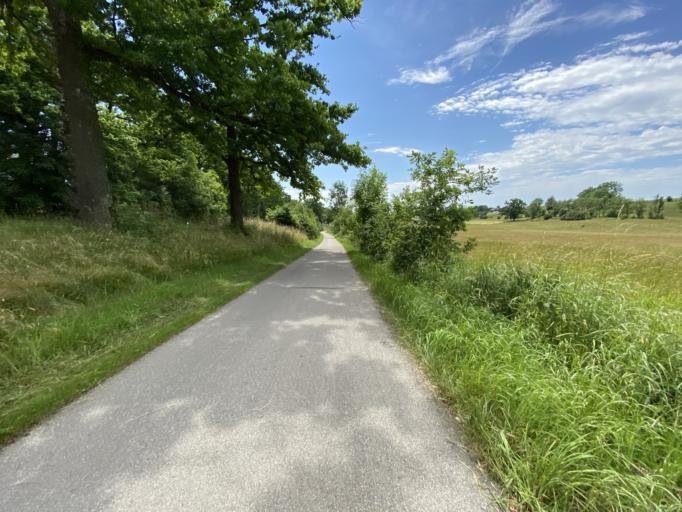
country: DE
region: Bavaria
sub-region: Upper Bavaria
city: Wessling
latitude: 48.0591
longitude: 11.2357
